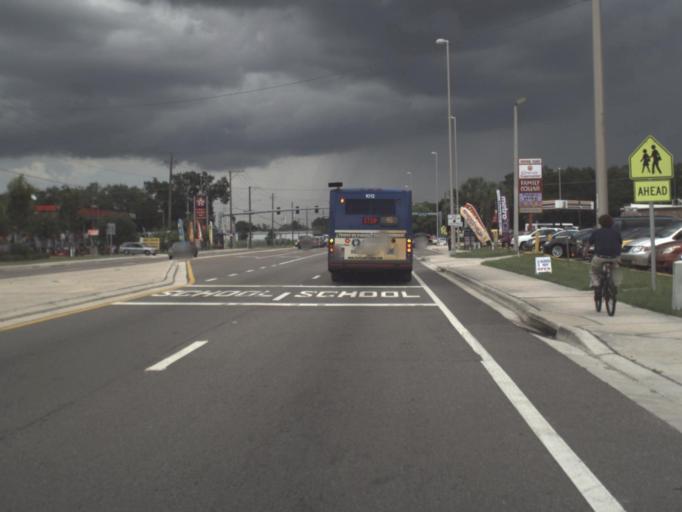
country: US
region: Florida
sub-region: Hillsborough County
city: Palm River-Clair Mel
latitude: 27.9226
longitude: -82.3706
